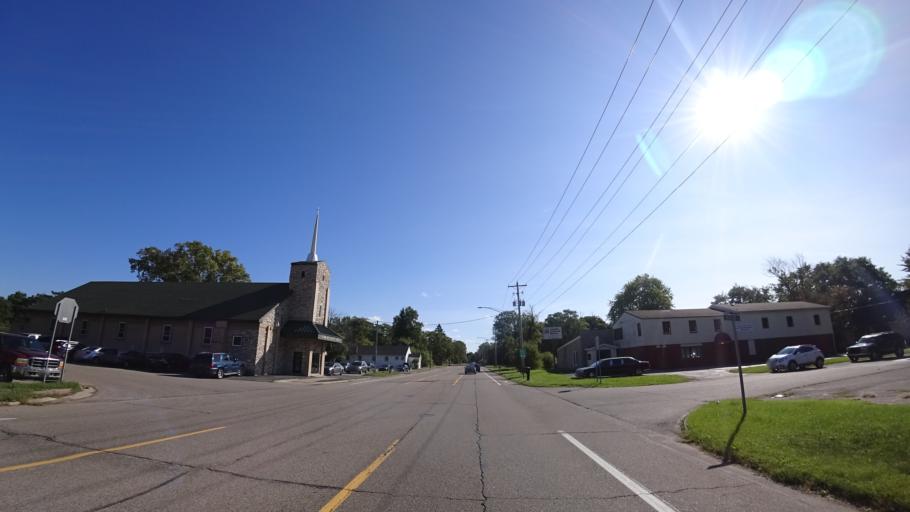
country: US
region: Michigan
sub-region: Berrien County
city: Benton Harbor
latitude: 42.1178
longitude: -86.4324
